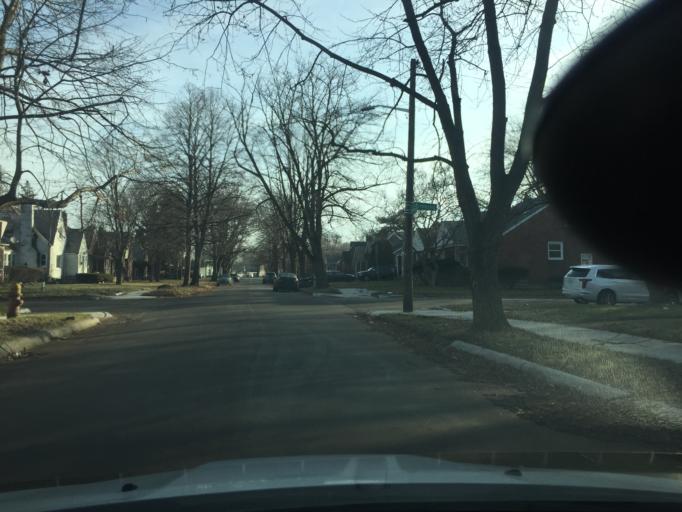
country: US
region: Michigan
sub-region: Wayne County
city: Harper Woods
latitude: 42.4339
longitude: -82.9560
